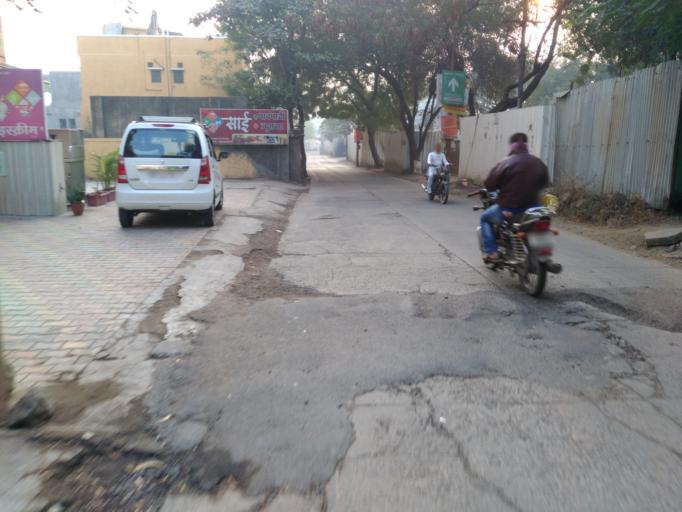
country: IN
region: Maharashtra
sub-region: Pune Division
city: Pune
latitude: 18.4591
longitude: 73.9103
